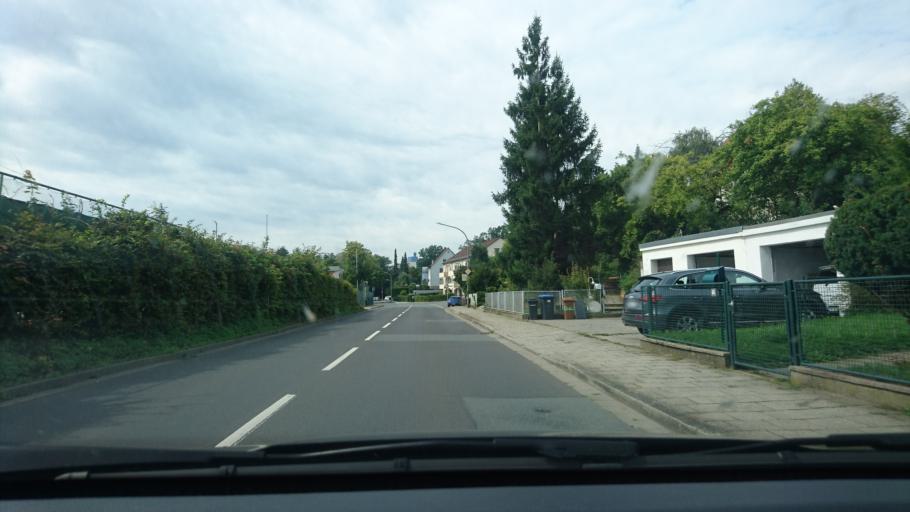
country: DE
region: Bavaria
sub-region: Upper Franconia
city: Bayreuth
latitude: 49.9420
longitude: 11.5546
